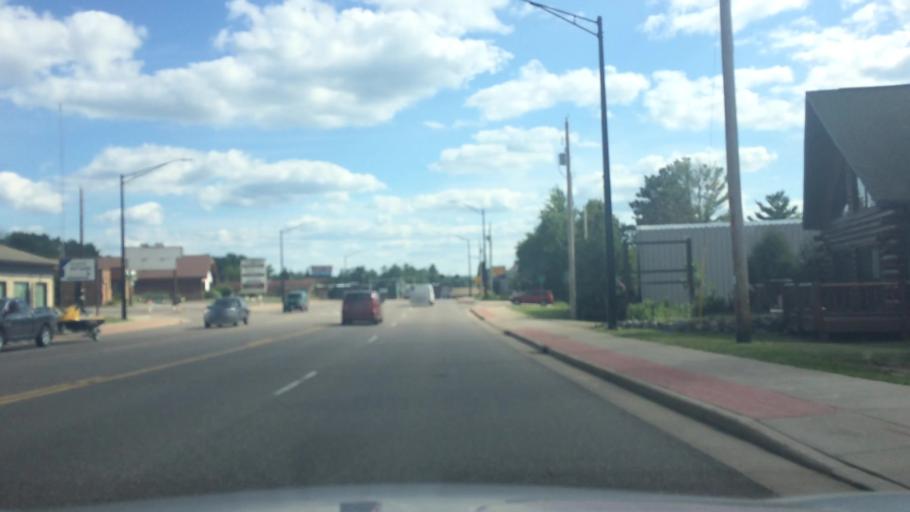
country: US
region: Wisconsin
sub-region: Vilas County
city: Lac du Flambeau
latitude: 45.8801
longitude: -89.7032
